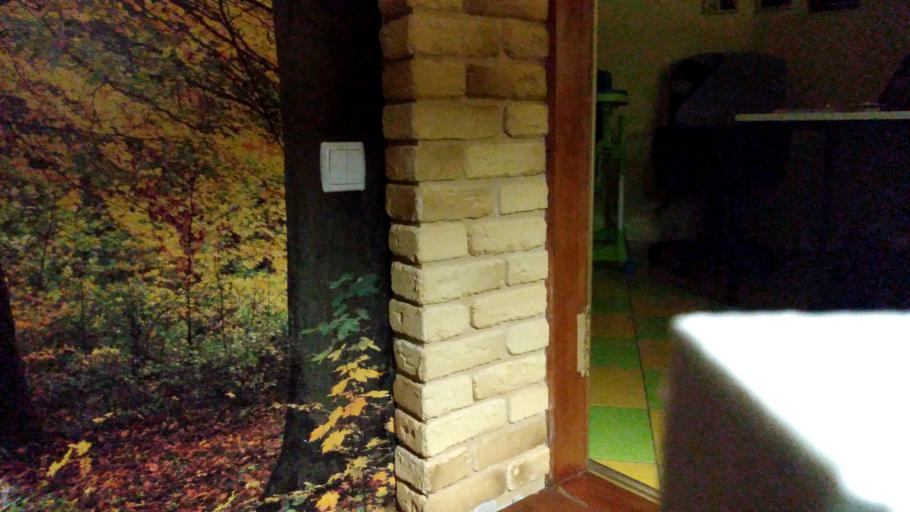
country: RU
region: Vologda
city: Lipin Bor
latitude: 60.7898
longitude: 38.0368
